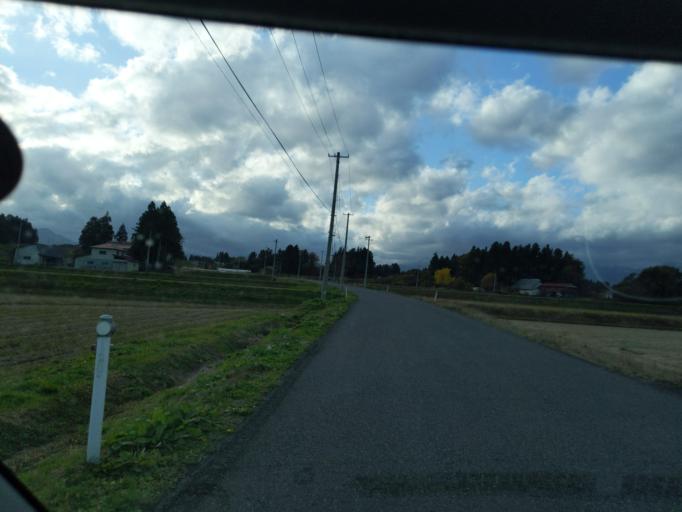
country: JP
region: Iwate
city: Mizusawa
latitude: 39.1094
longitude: 141.0307
